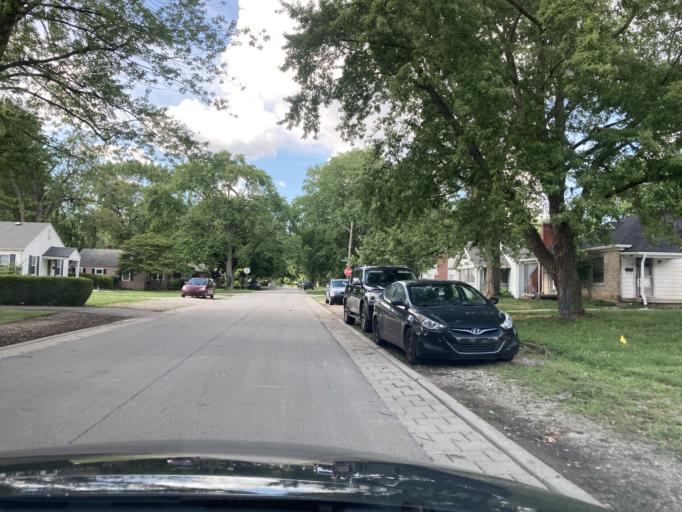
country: US
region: Indiana
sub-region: Marion County
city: Broad Ripple
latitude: 39.8599
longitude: -86.1340
